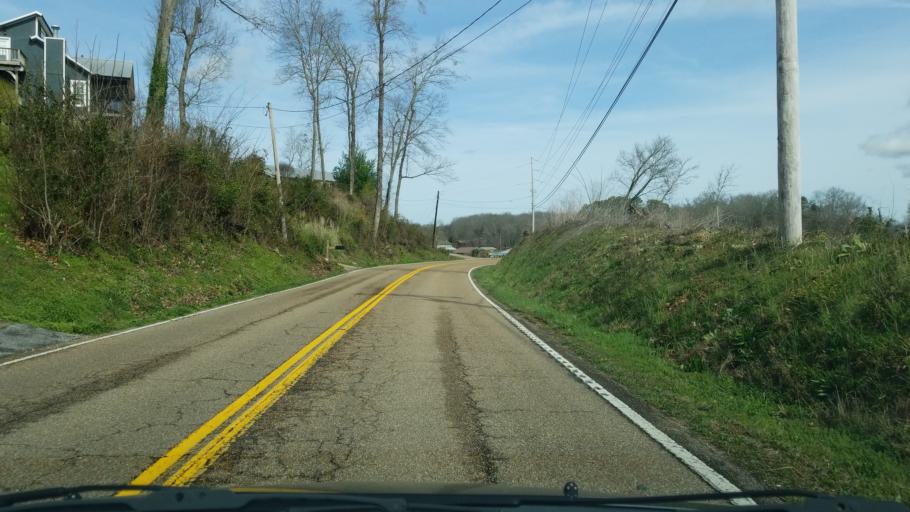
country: US
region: Tennessee
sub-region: Hamilton County
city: Lakesite
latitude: 35.1556
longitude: -85.0617
